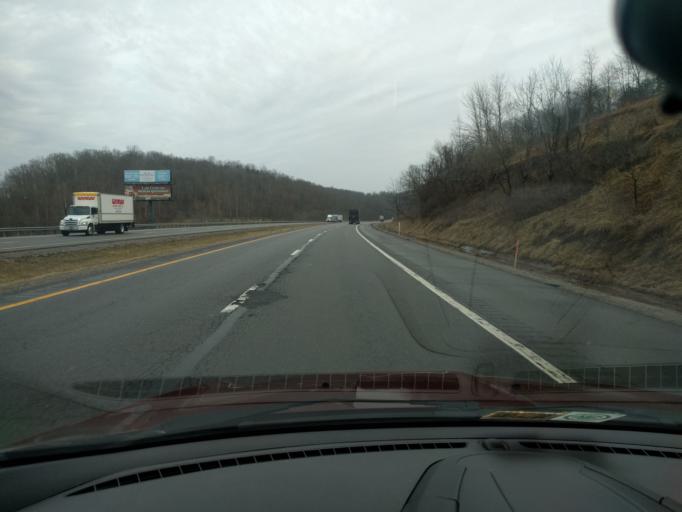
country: US
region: West Virginia
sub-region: Jackson County
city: Ravenswood
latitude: 39.0142
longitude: -81.6216
